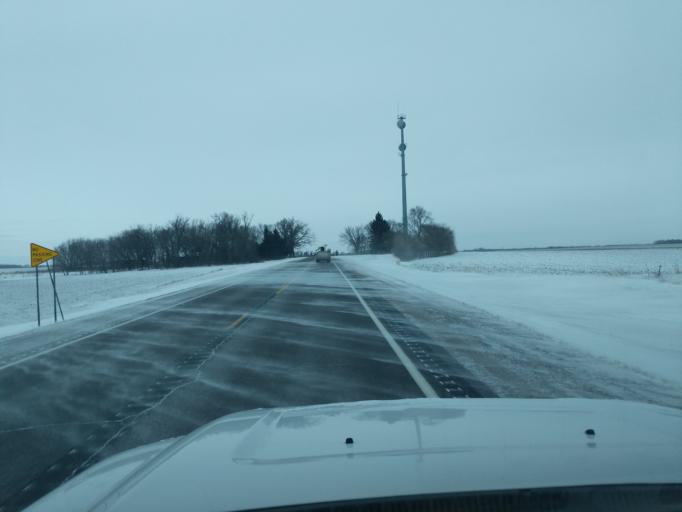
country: US
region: Minnesota
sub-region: Redwood County
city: Redwood Falls
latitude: 44.6002
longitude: -94.9944
